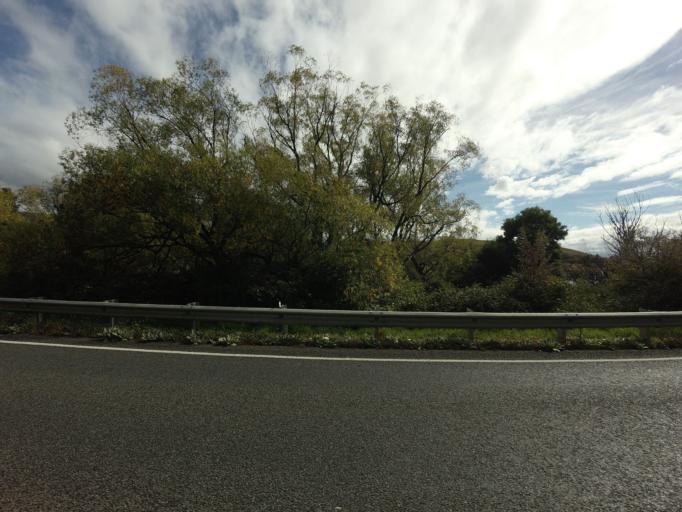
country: AU
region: Tasmania
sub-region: Derwent Valley
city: New Norfolk
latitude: -42.7301
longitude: 146.9568
